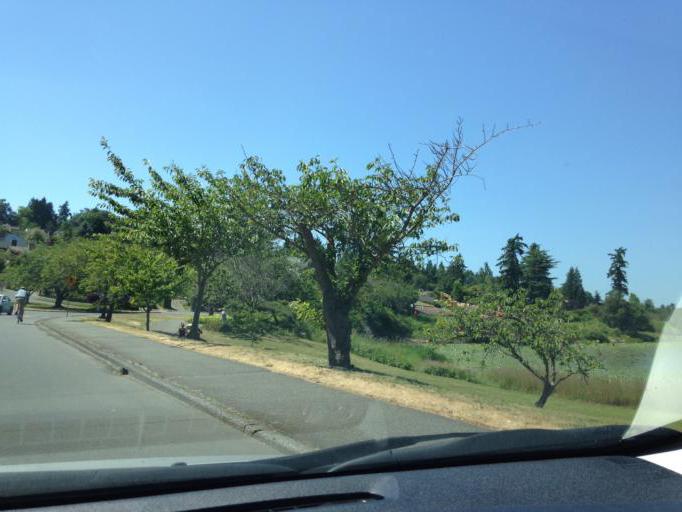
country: US
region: Washington
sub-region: King County
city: Mercer Island
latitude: 47.5510
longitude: -122.2587
